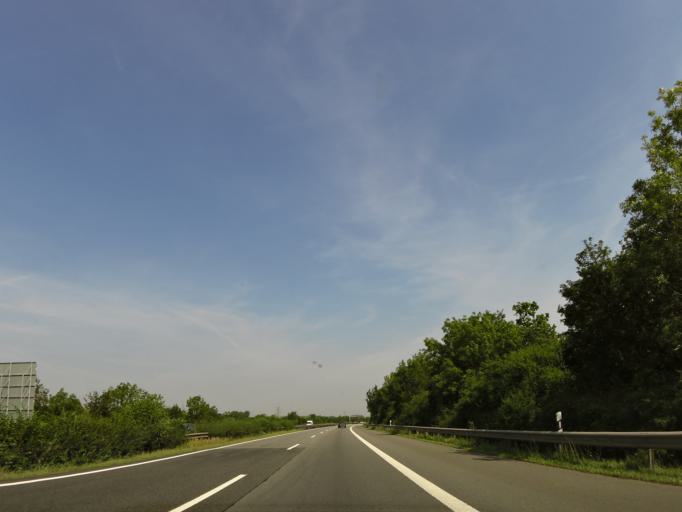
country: DE
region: Rheinland-Pfalz
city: Alzey
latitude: 49.7587
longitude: 8.1195
